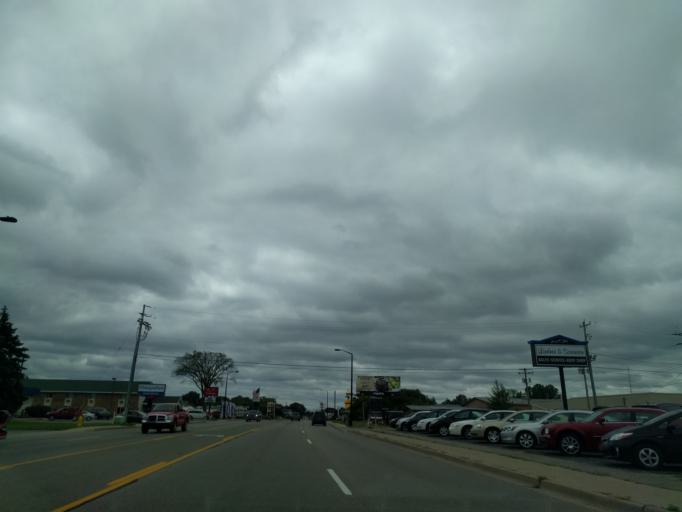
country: US
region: Michigan
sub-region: Menominee County
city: Menominee
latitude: 45.1228
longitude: -87.6133
